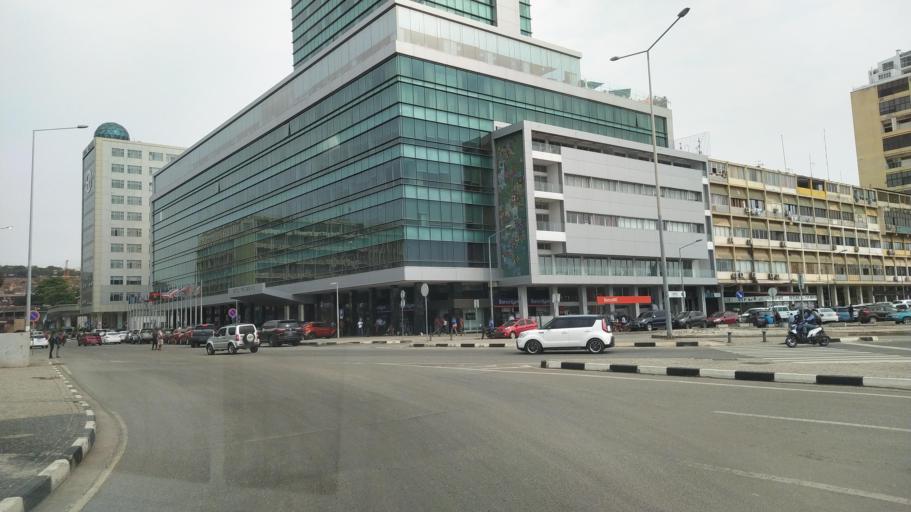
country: AO
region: Luanda
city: Luanda
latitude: -8.8028
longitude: 13.2418
